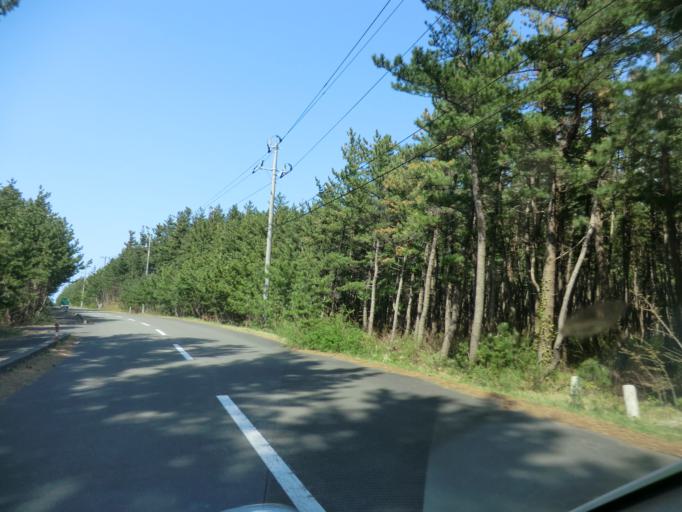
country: JP
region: Aomori
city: Mutsu
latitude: 41.4150
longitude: 141.4488
